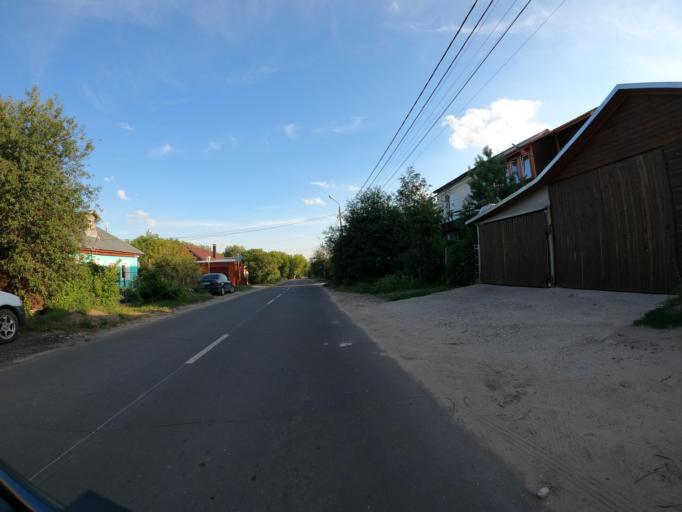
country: RU
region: Moskovskaya
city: Raduzhnyy
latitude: 55.1064
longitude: 38.7274
